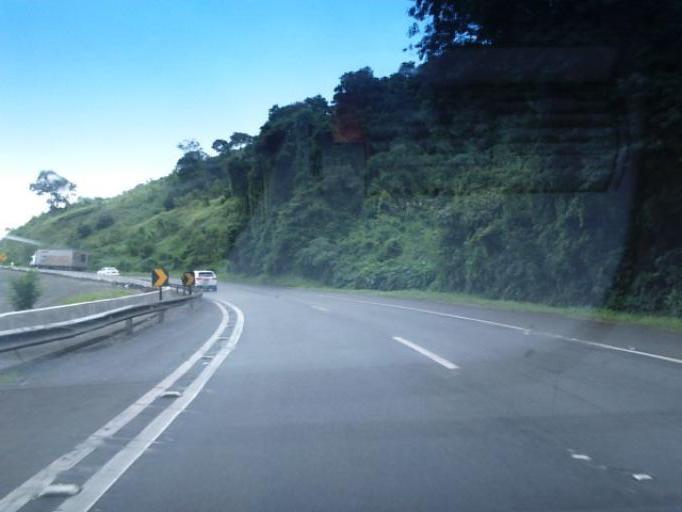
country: BR
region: Sao Paulo
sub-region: Cajati
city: Cajati
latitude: -24.9675
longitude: -48.4779
